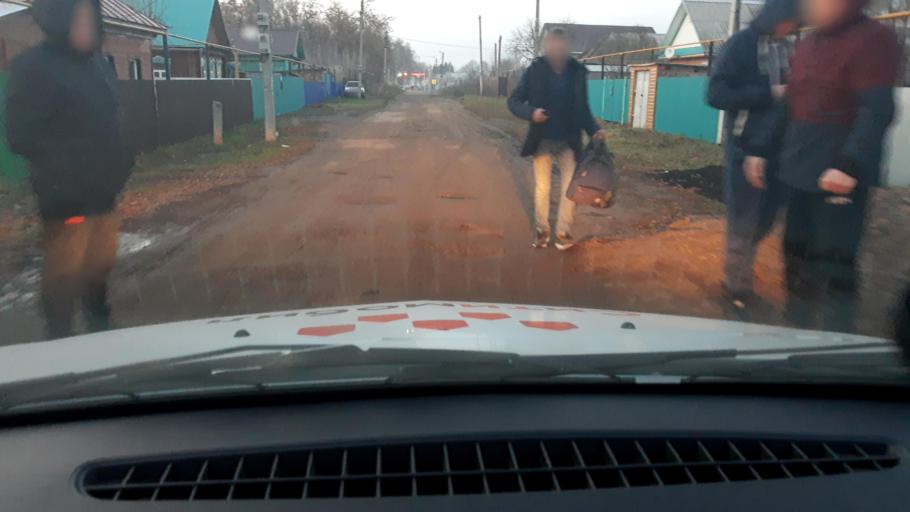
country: RU
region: Bashkortostan
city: Iglino
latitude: 54.7738
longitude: 56.2250
